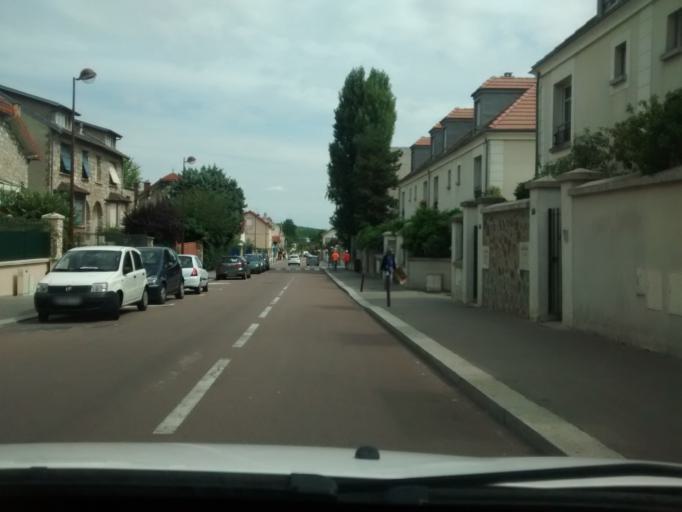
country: FR
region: Ile-de-France
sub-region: Departement des Yvelines
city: Versailles
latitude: 48.7923
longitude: 2.1471
